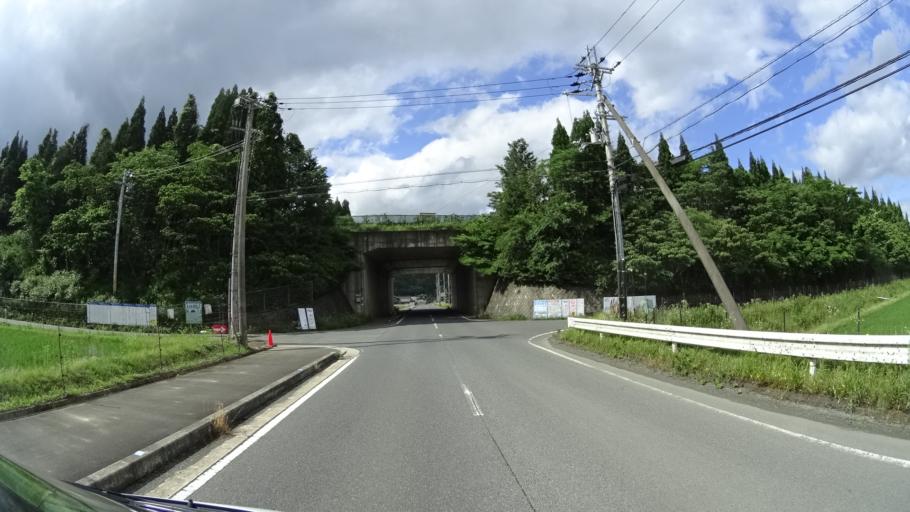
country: JP
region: Kyoto
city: Ayabe
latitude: 35.3236
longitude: 135.2077
